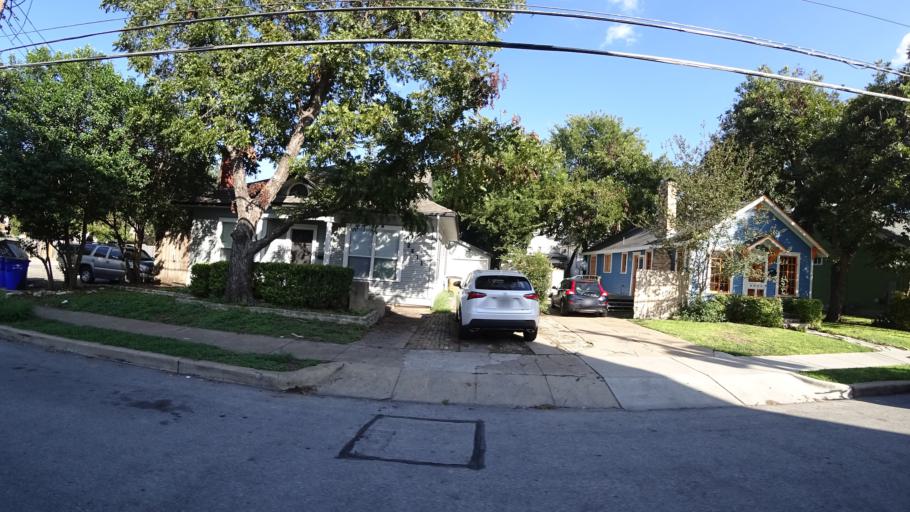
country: US
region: Texas
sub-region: Travis County
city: Austin
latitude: 30.2917
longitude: -97.7453
